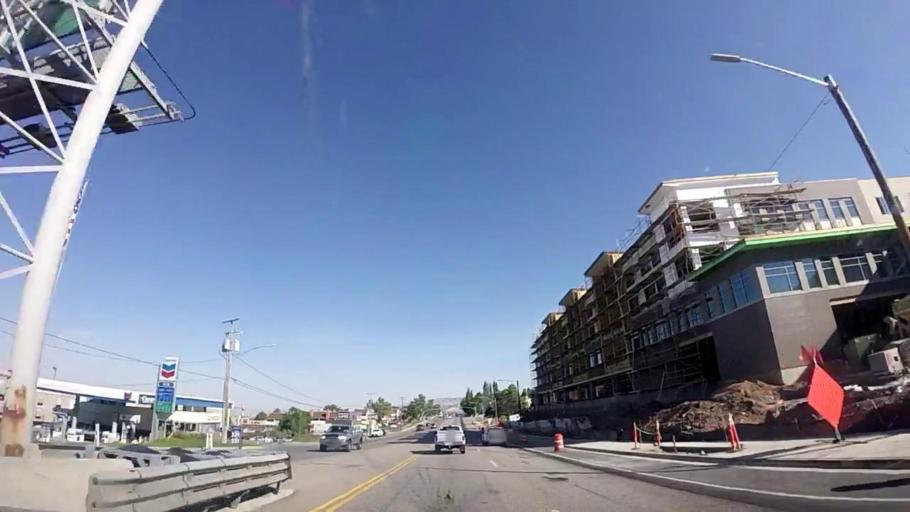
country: US
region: Utah
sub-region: Salt Lake County
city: Canyon Rim
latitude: 40.7196
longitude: -111.8103
